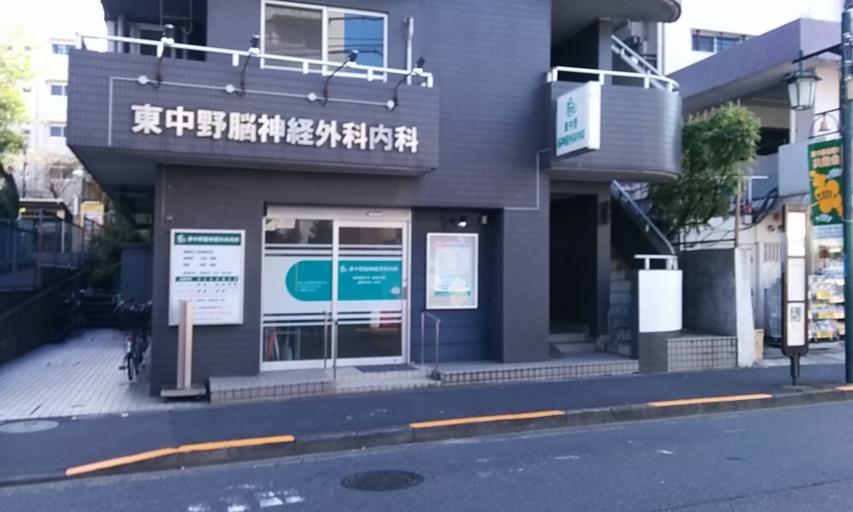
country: JP
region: Tokyo
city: Tokyo
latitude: 35.7098
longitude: 139.6883
